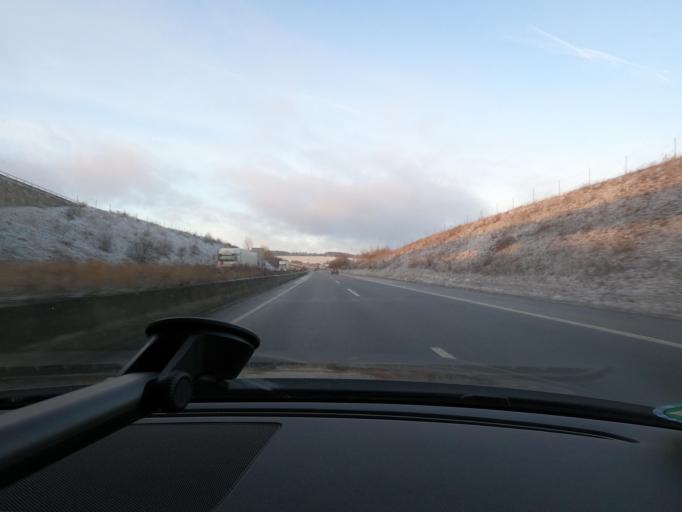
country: DE
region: Thuringia
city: Leinefelde
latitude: 51.4001
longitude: 10.3316
